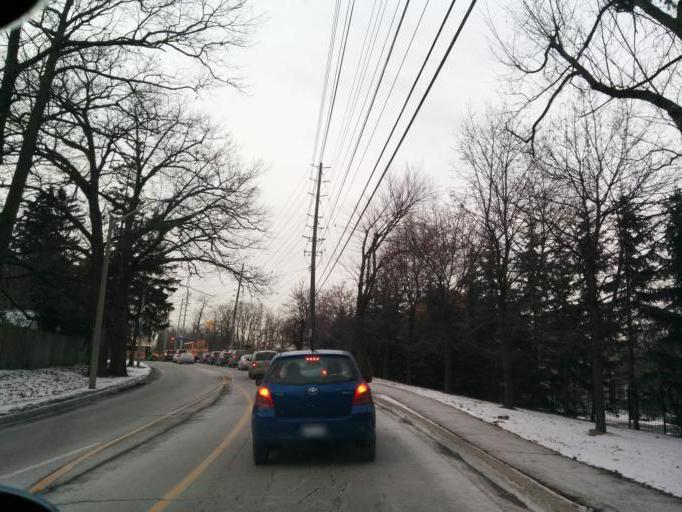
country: CA
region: Ontario
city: Mississauga
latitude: 43.5527
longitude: -79.6742
